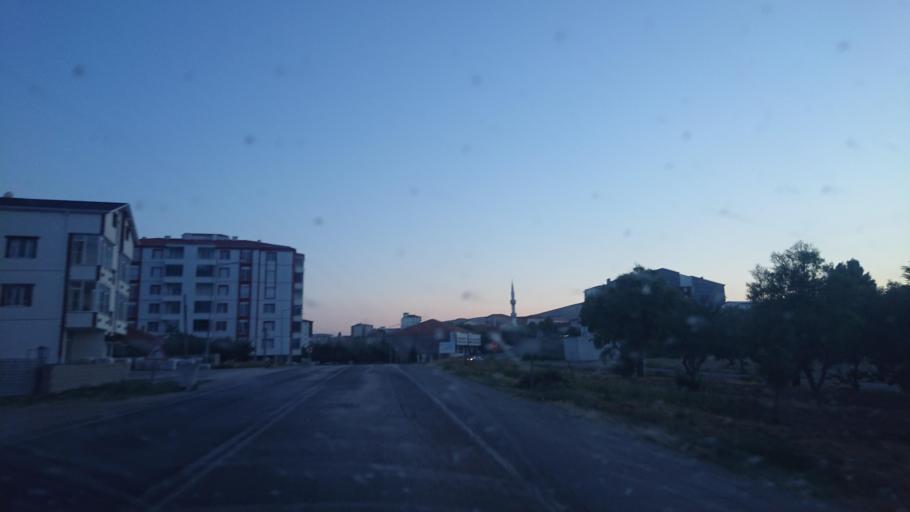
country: TR
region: Aksaray
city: Ortakoy
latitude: 38.7434
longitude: 34.0497
